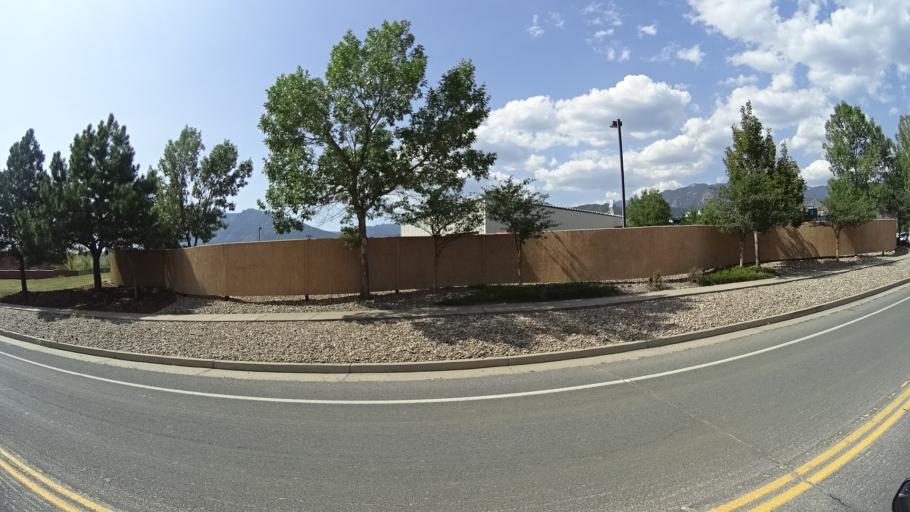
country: US
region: Colorado
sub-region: El Paso County
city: Colorado Springs
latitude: 38.8252
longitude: -104.8448
